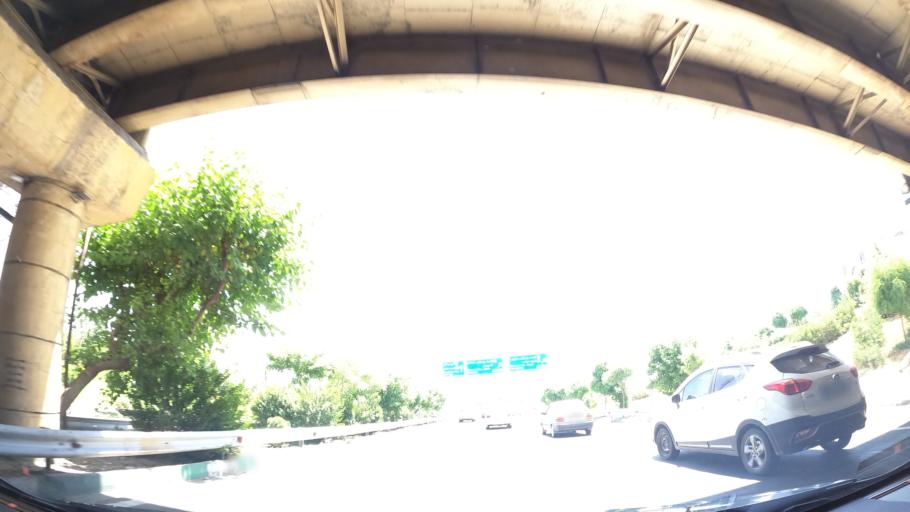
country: IR
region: Tehran
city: Tajrish
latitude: 35.7785
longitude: 51.3854
